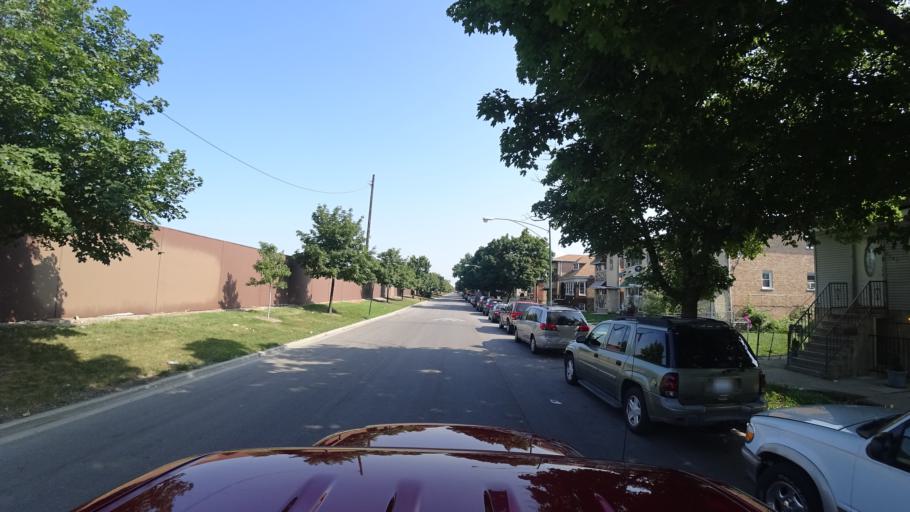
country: US
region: Illinois
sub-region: Cook County
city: Cicero
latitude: 41.8101
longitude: -87.7125
